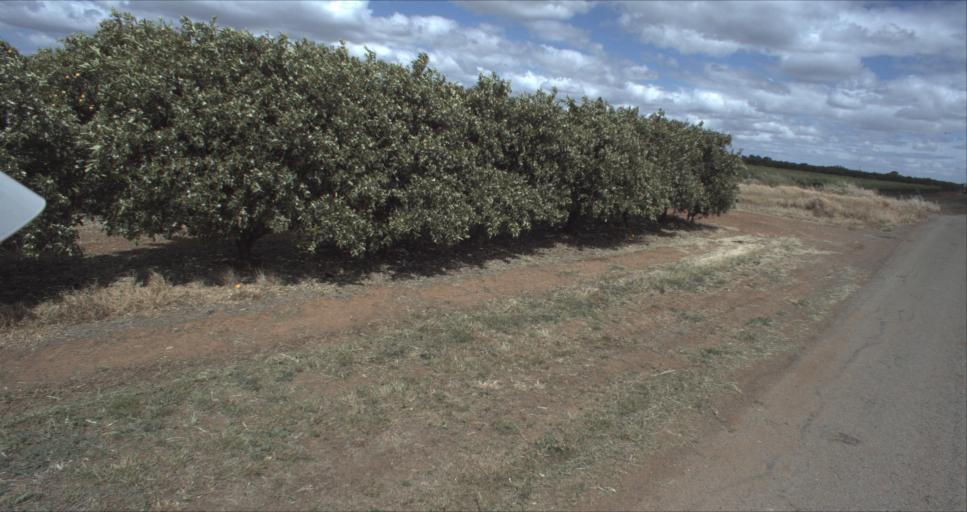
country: AU
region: New South Wales
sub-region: Leeton
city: Leeton
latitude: -34.5851
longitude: 146.3915
